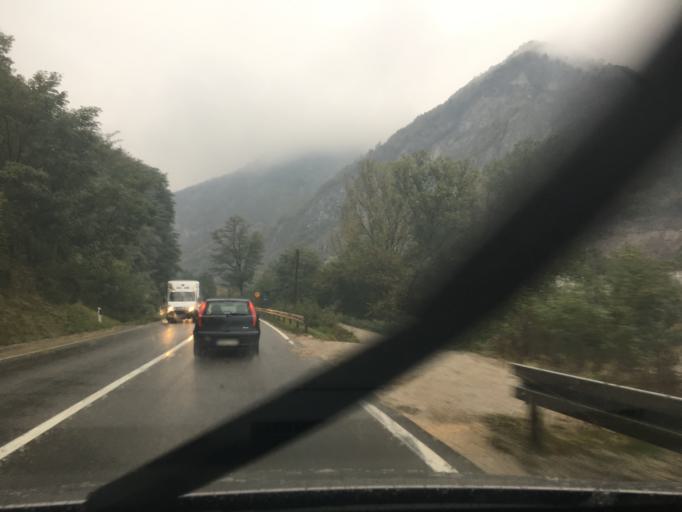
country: RS
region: Central Serbia
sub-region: Pcinjski Okrug
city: Vladicin Han
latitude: 42.7524
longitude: 22.0807
